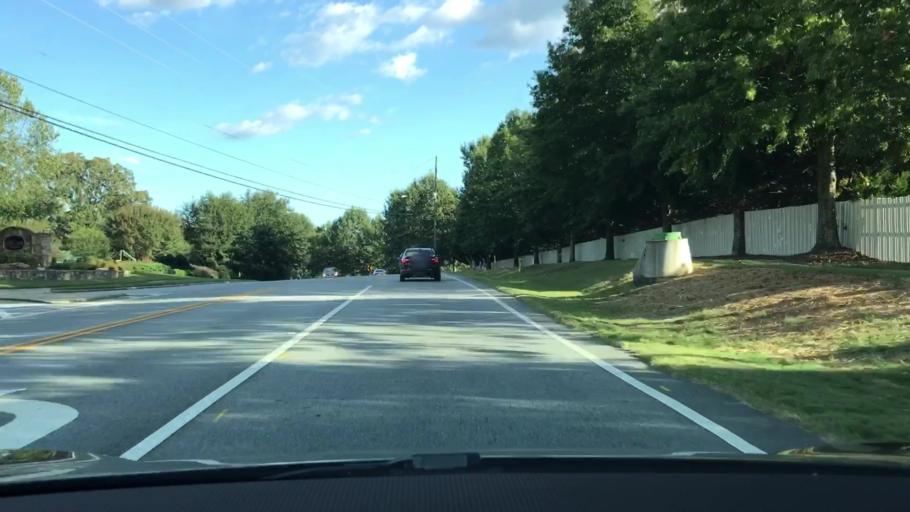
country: US
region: Georgia
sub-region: Gwinnett County
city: Dacula
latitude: 34.0419
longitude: -83.9200
